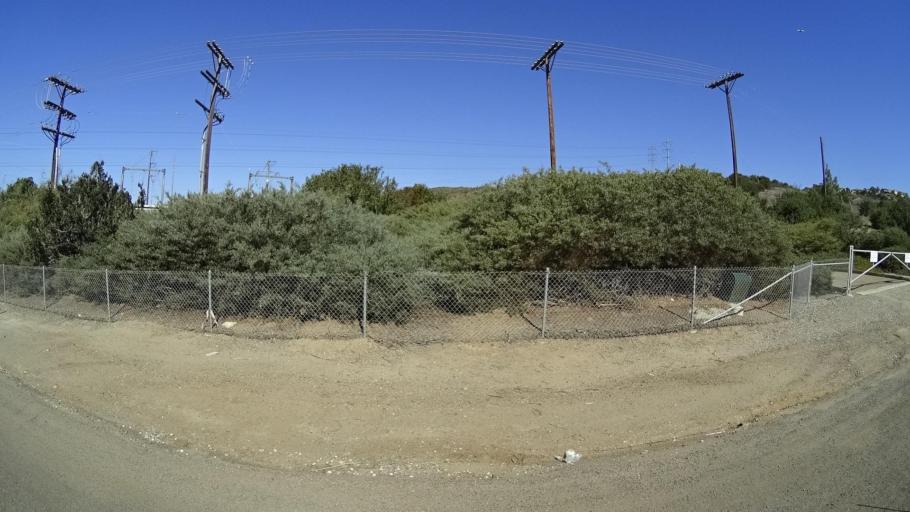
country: US
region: California
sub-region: San Diego County
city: Bonita
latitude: 32.6645
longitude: -116.9862
